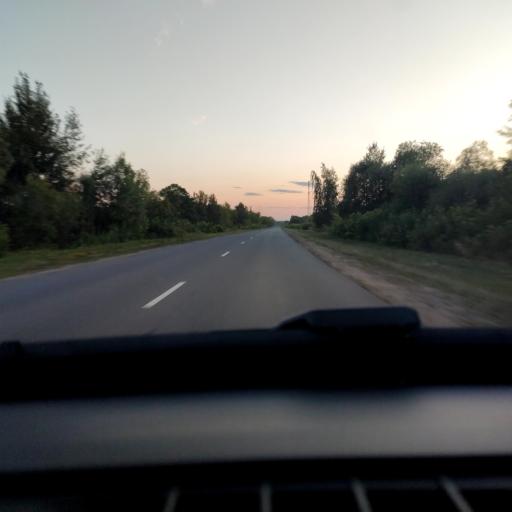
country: RU
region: Lipetsk
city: Zadonsk
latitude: 52.2959
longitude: 38.7845
